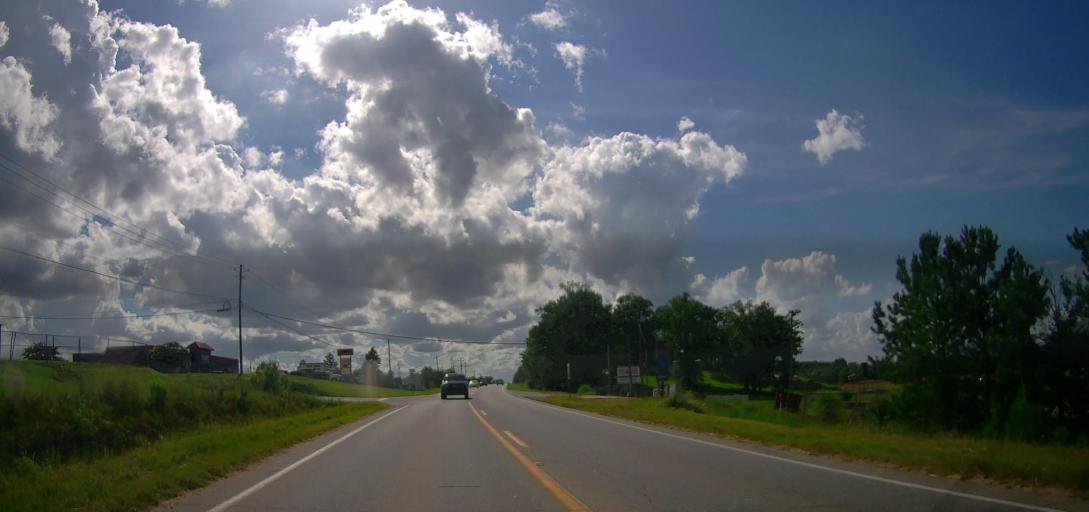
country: US
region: Alabama
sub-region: Russell County
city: Ladonia
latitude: 32.4603
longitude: -85.1455
